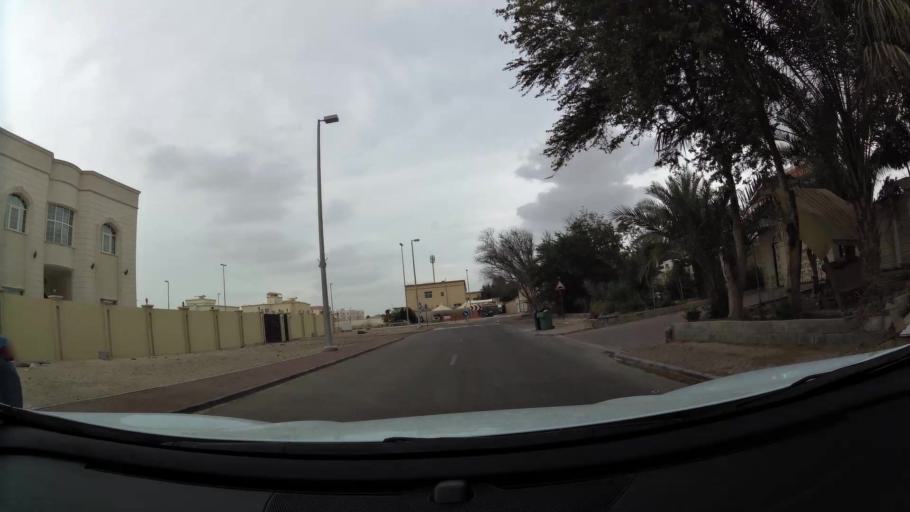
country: AE
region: Abu Dhabi
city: Abu Dhabi
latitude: 24.3738
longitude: 54.6434
